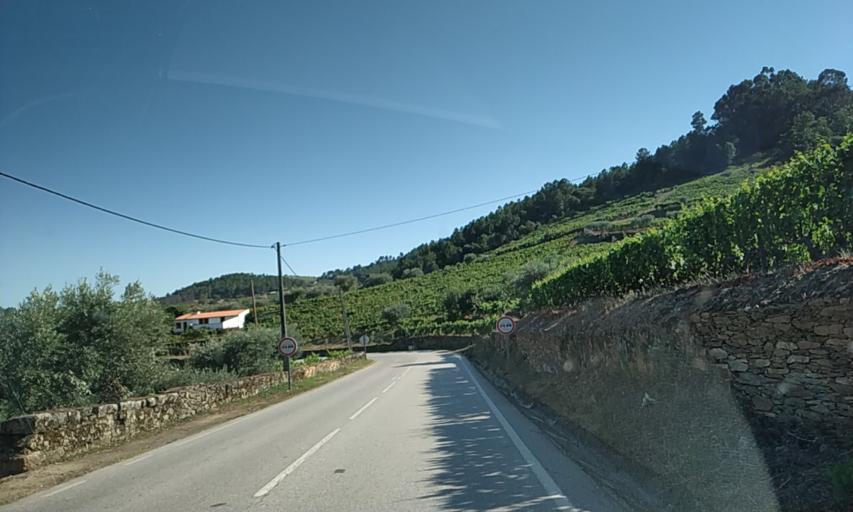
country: PT
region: Viseu
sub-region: Sao Joao da Pesqueira
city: Sao Joao da Pesqueira
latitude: 41.2575
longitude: -7.4407
